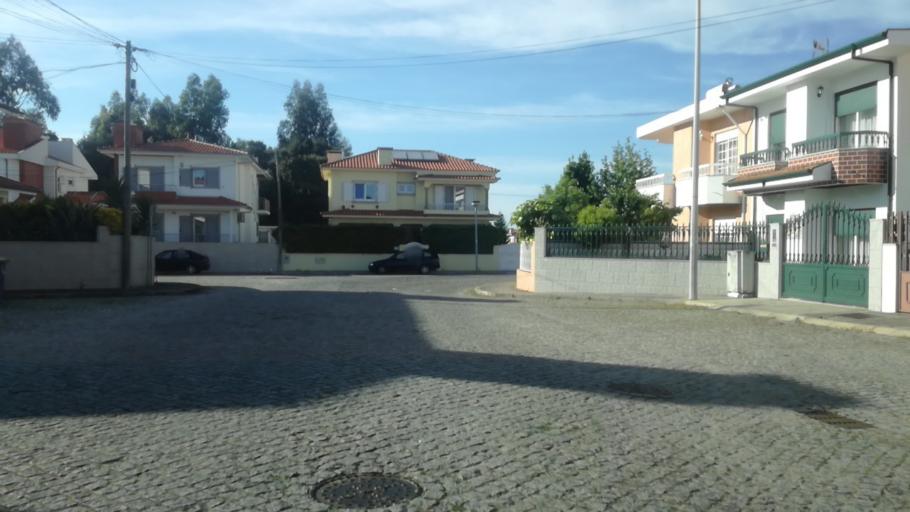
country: PT
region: Porto
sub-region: Maia
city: Gemunde
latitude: 41.2571
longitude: -8.6684
